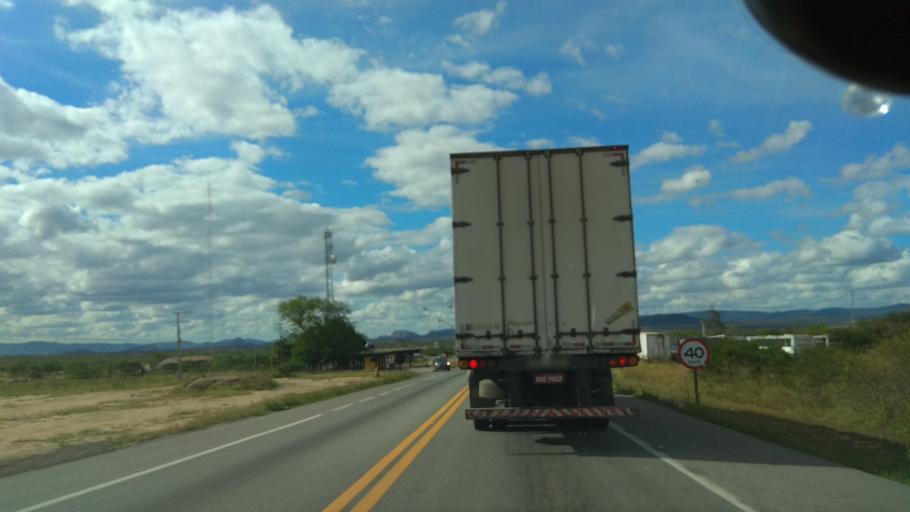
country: BR
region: Bahia
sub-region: Amargosa
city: Amargosa
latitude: -12.8573
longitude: -39.8486
